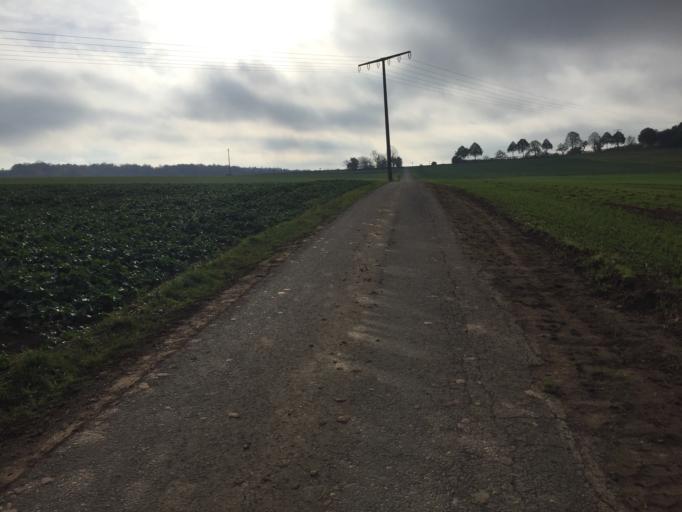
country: DE
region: Hesse
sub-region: Regierungsbezirk Giessen
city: Grunberg
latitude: 50.5975
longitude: 8.9775
